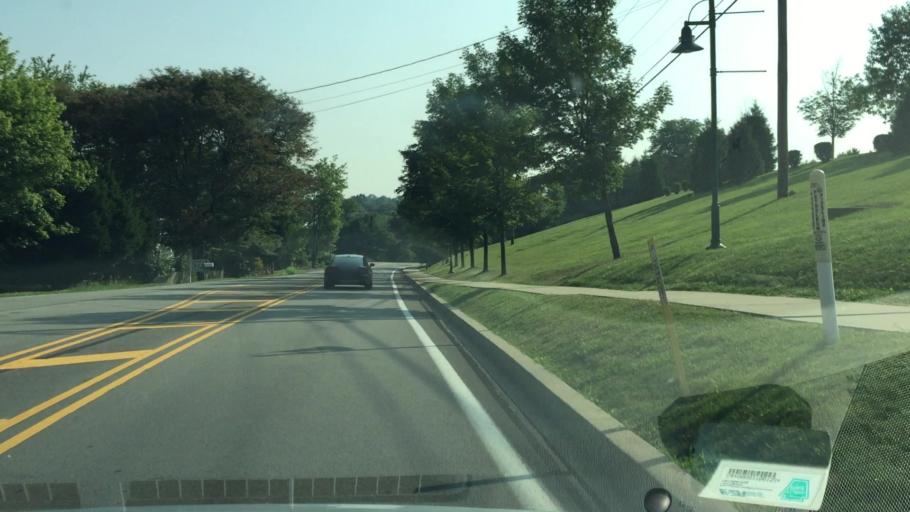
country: US
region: Pennsylvania
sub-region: Allegheny County
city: Bradford Woods
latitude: 40.6346
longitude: -80.0578
